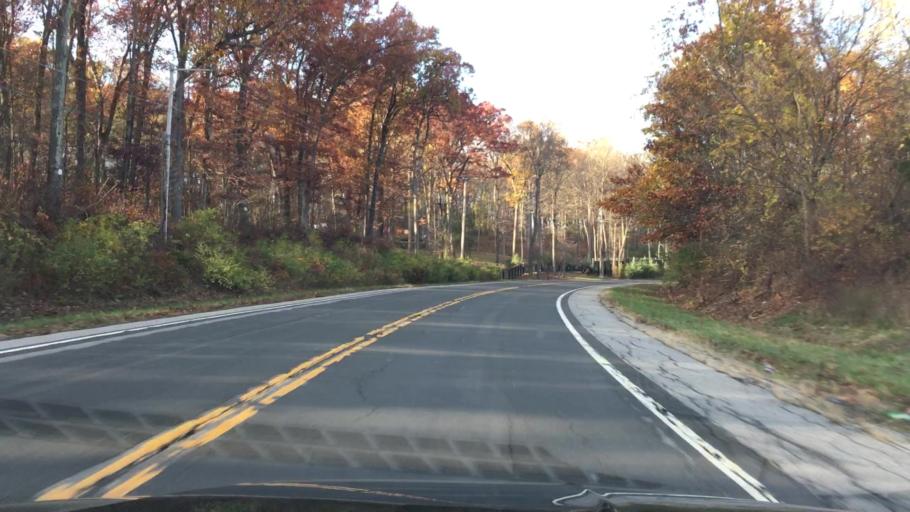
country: US
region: New York
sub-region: Dutchess County
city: Myers Corner
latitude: 41.6085
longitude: -73.8481
